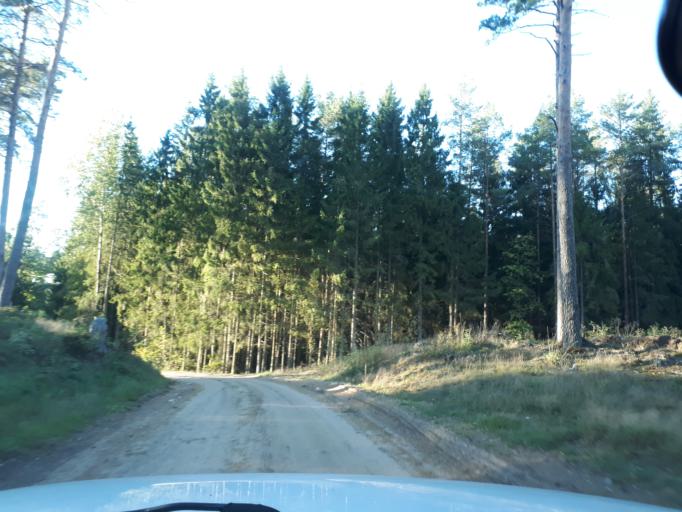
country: LT
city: Kulautuva
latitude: 54.9317
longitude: 23.5856
